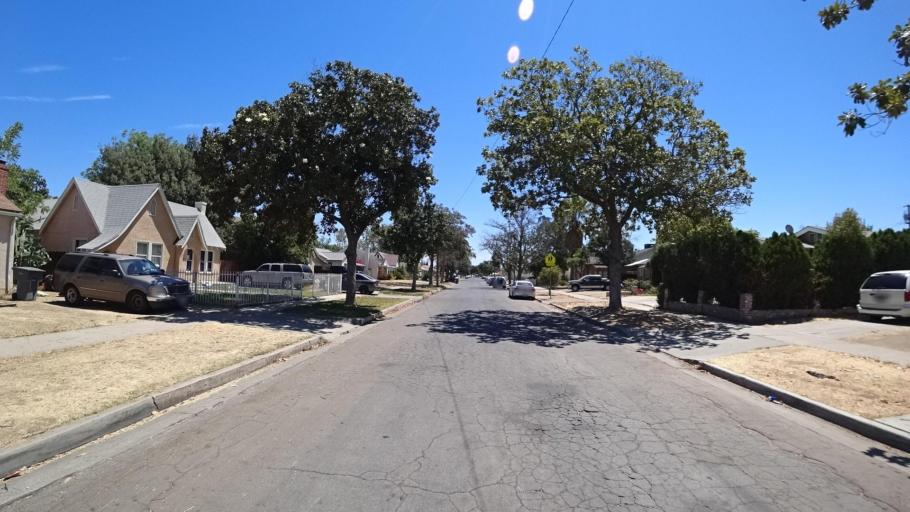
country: US
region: California
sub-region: Fresno County
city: Fresno
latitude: 36.7450
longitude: -119.7420
